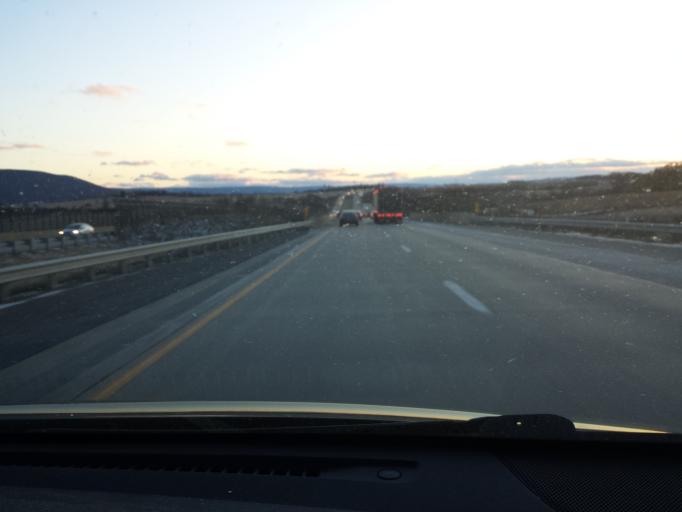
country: US
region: Pennsylvania
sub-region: Centre County
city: Pleasant Gap
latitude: 40.8669
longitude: -77.7847
